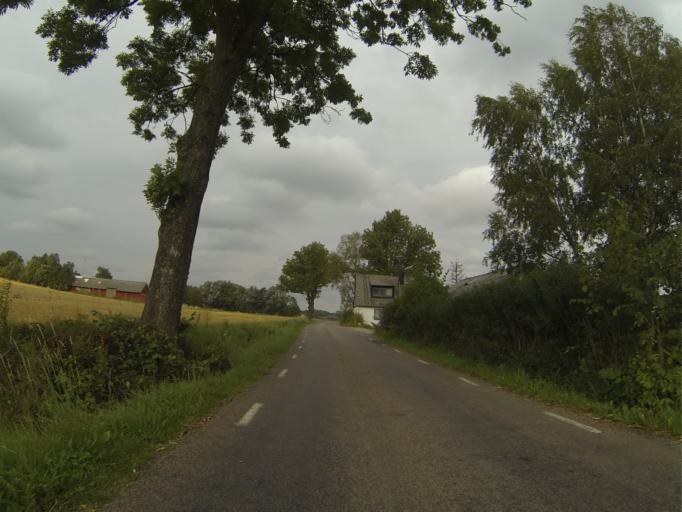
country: SE
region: Skane
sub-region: Eslovs Kommun
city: Eslov
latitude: 55.7647
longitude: 13.3123
